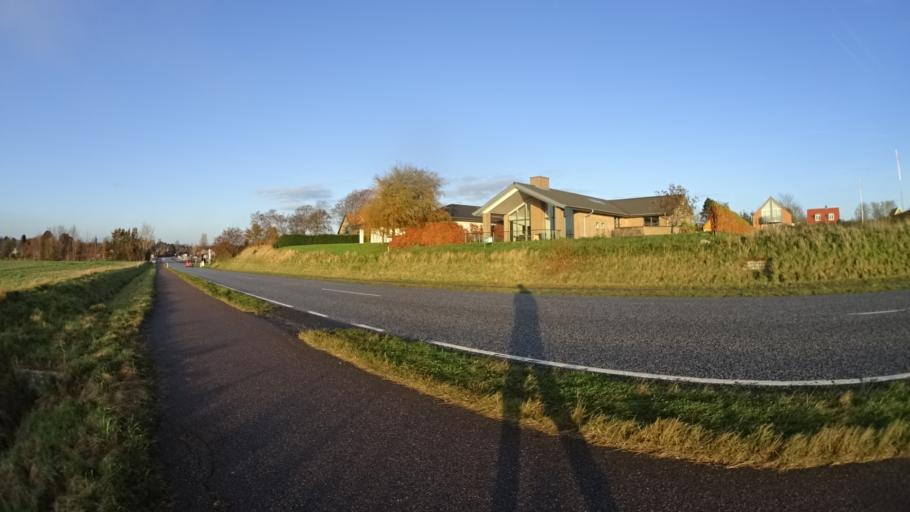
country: DK
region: Central Jutland
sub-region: Arhus Kommune
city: Beder
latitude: 56.0205
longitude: 10.2613
